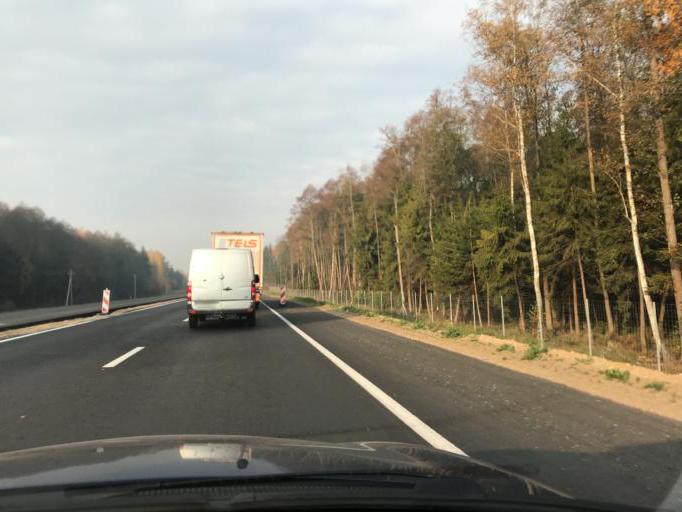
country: BY
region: Grodnenskaya
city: Lida
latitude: 53.8288
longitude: 25.4080
